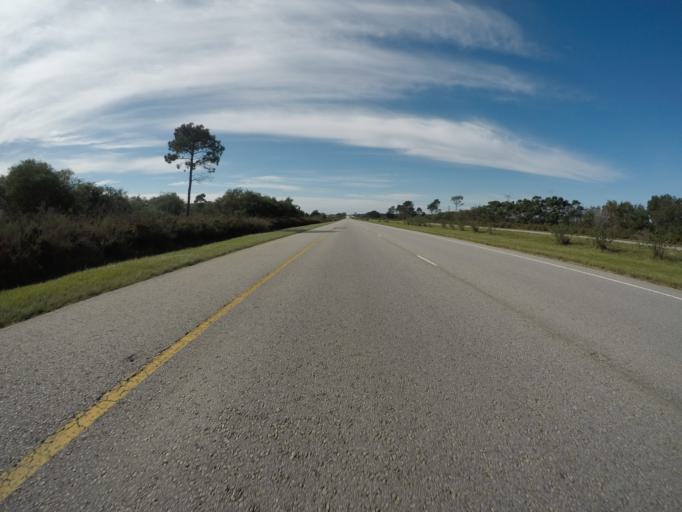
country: ZA
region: Eastern Cape
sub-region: Nelson Mandela Bay Metropolitan Municipality
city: Uitenhage
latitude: -33.9092
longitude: 25.2511
